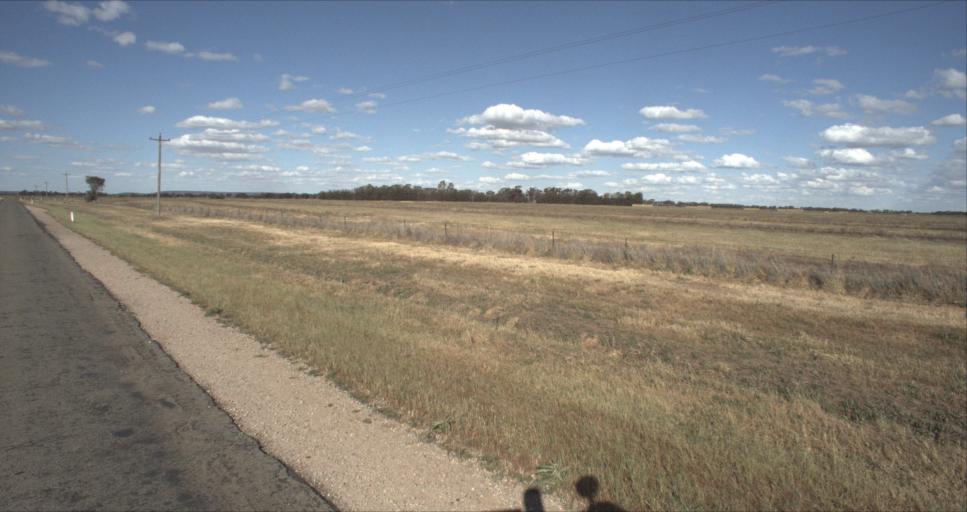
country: AU
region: New South Wales
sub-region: Leeton
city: Leeton
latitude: -34.4573
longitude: 146.2715
